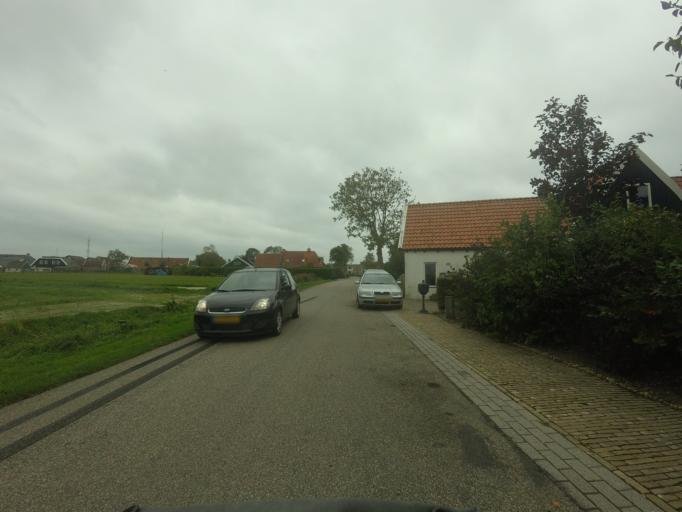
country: NL
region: Friesland
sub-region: Gemeente Dongeradeel
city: Holwerd
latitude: 53.3524
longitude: 5.8649
